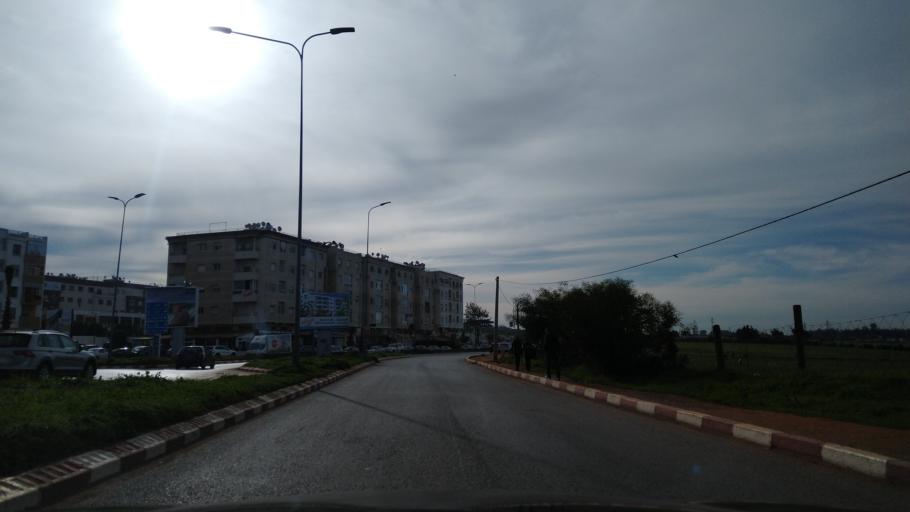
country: MA
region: Rabat-Sale-Zemmour-Zaer
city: Sale
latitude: 33.9886
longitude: -6.7396
